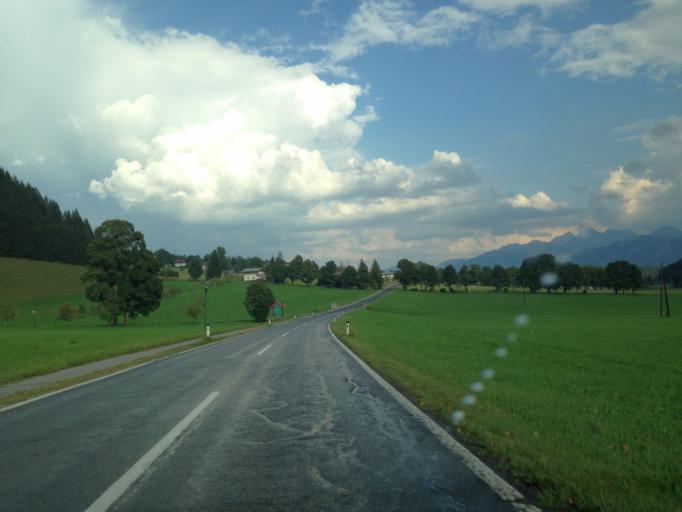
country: AT
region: Styria
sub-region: Politischer Bezirk Liezen
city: Schladming
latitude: 47.4284
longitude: 13.6136
